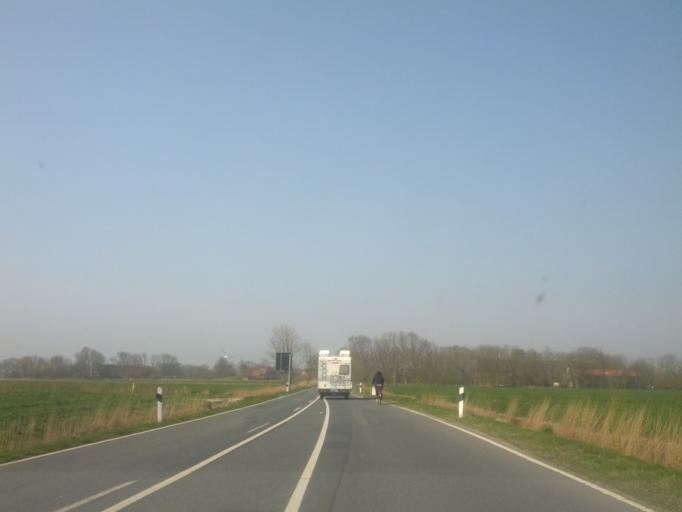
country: DE
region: Lower Saxony
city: Dornum
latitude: 53.6687
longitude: 7.3648
